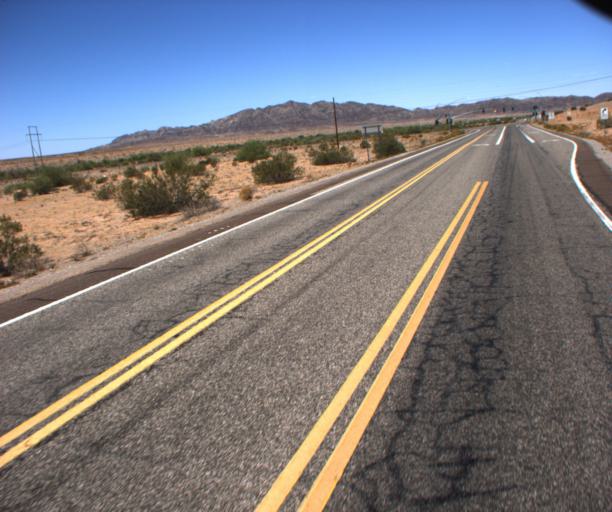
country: US
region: Arizona
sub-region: La Paz County
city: Parker
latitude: 33.9942
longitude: -114.2144
